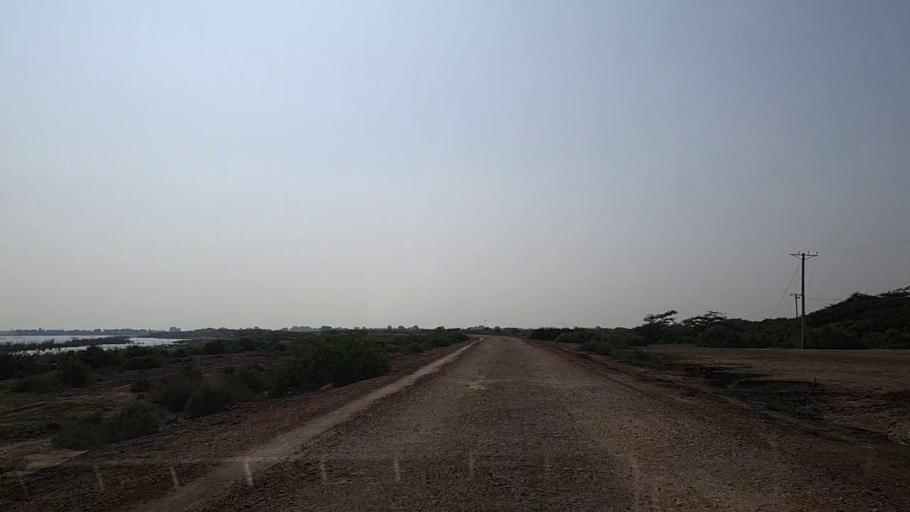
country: PK
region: Sindh
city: Mirpur Sakro
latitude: 24.6398
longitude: 67.6641
